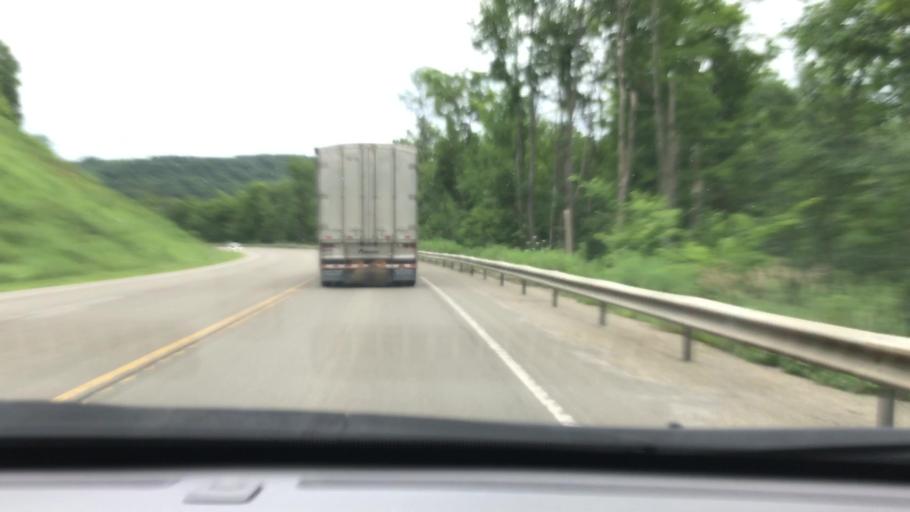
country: US
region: Pennsylvania
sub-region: McKean County
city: Kane
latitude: 41.7581
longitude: -78.6982
